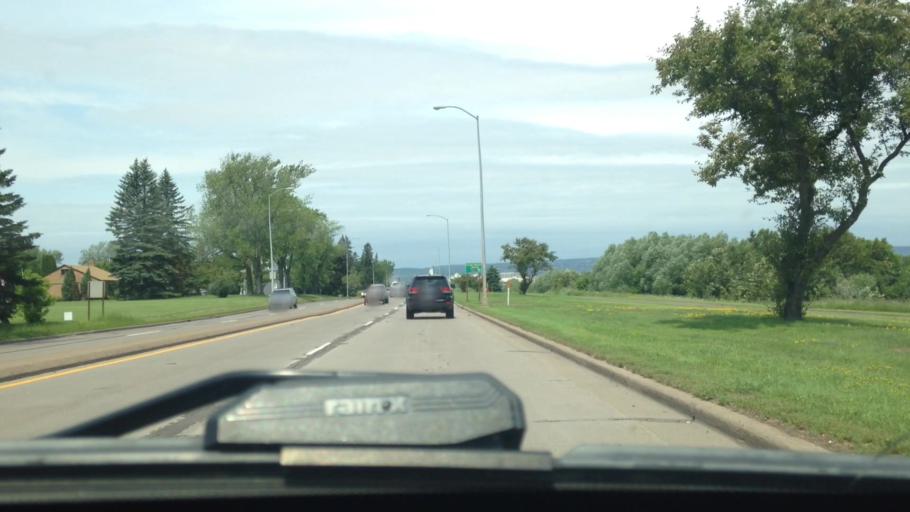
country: US
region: Wisconsin
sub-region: Douglas County
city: Superior
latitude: 46.7136
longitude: -92.0562
